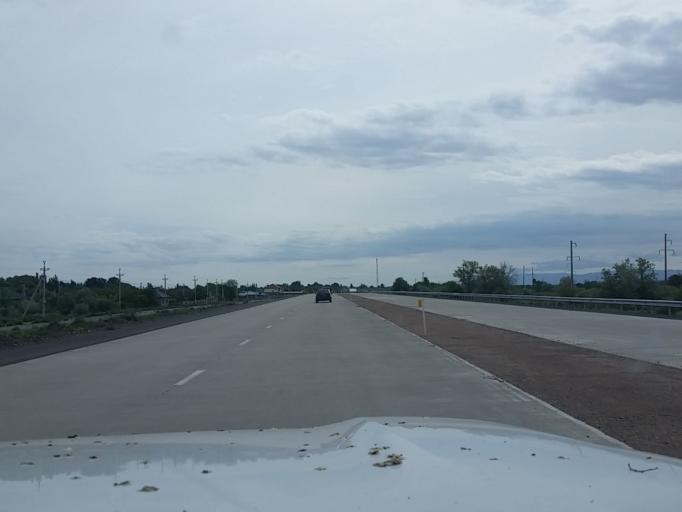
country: KZ
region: Almaty Oblysy
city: Turgen'
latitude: 43.5839
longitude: 78.2259
